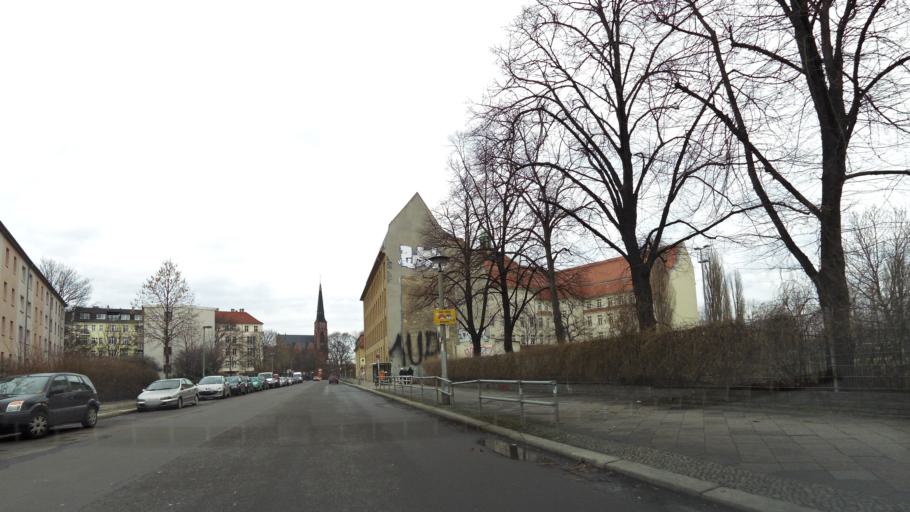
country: DE
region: Berlin
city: Treptow Bezirk
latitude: 52.5016
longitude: 13.4585
